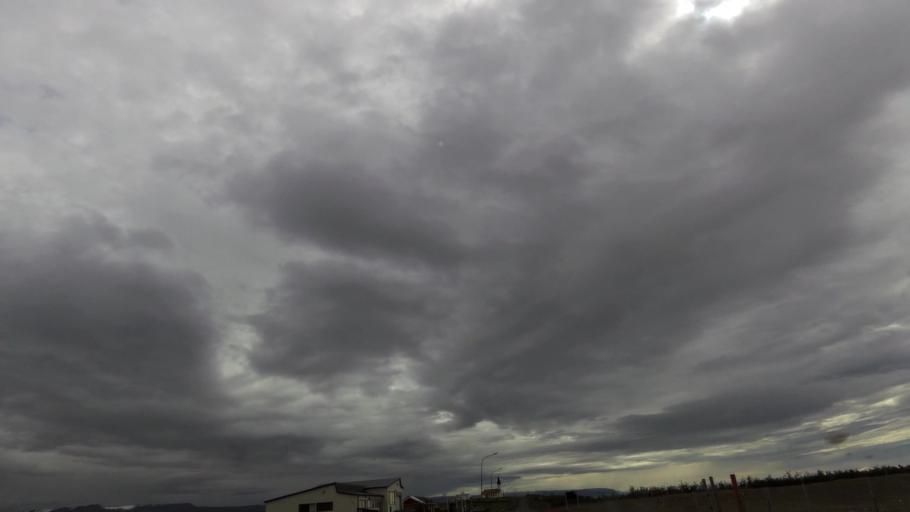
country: IS
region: West
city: Stykkisholmur
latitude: 65.4530
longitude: -22.2011
